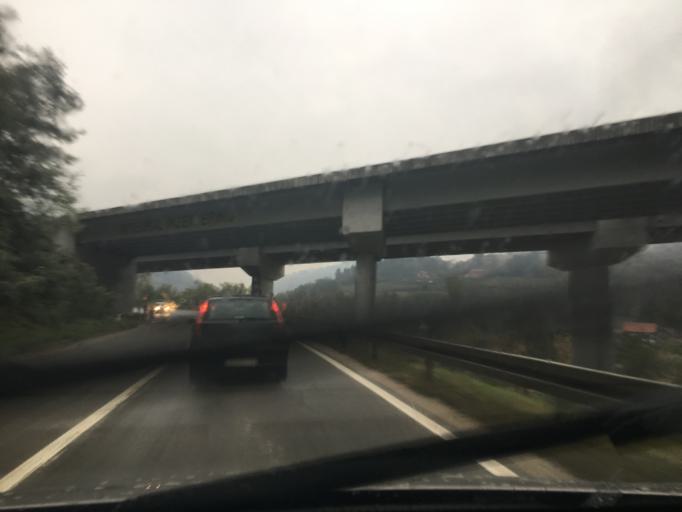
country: RS
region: Central Serbia
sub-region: Pcinjski Okrug
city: Vladicin Han
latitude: 42.7651
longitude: 22.0851
